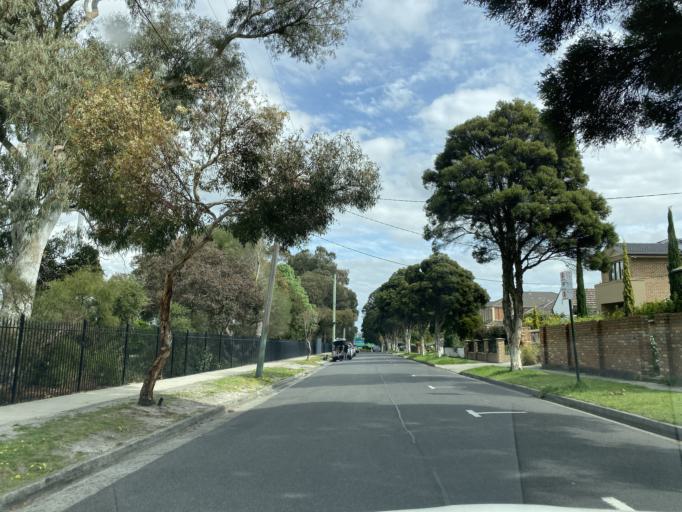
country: AU
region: Victoria
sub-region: Whitehorse
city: Burwood
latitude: -37.8478
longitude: 145.1039
